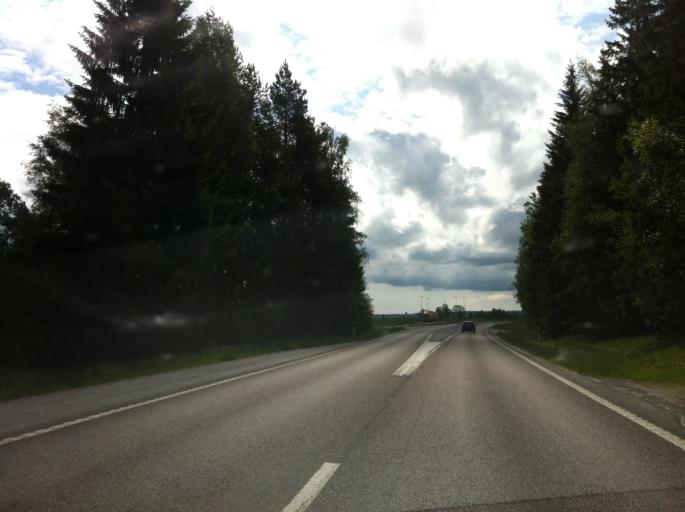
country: SE
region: Vaermland
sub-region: Karlstads Kommun
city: Edsvalla
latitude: 59.5466
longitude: 13.1970
